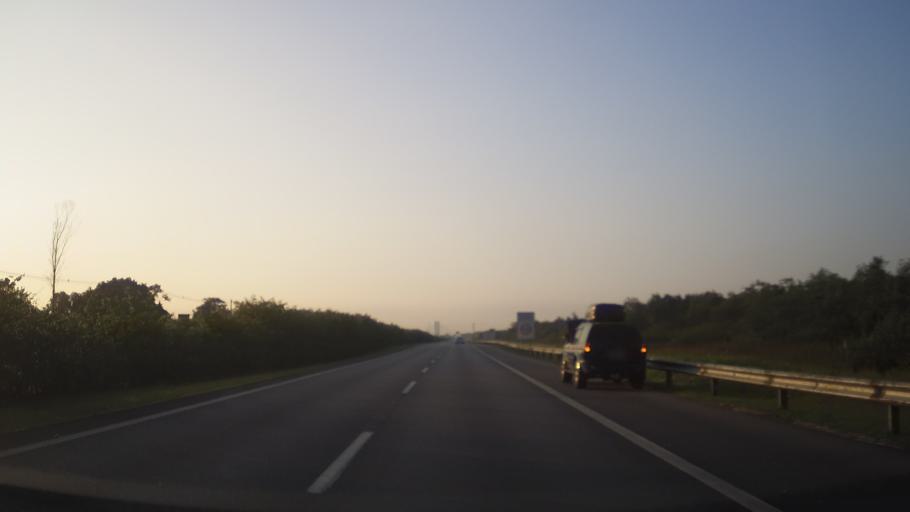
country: BR
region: Sao Paulo
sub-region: Cubatao
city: Cubatao
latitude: -23.9084
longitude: -46.4467
